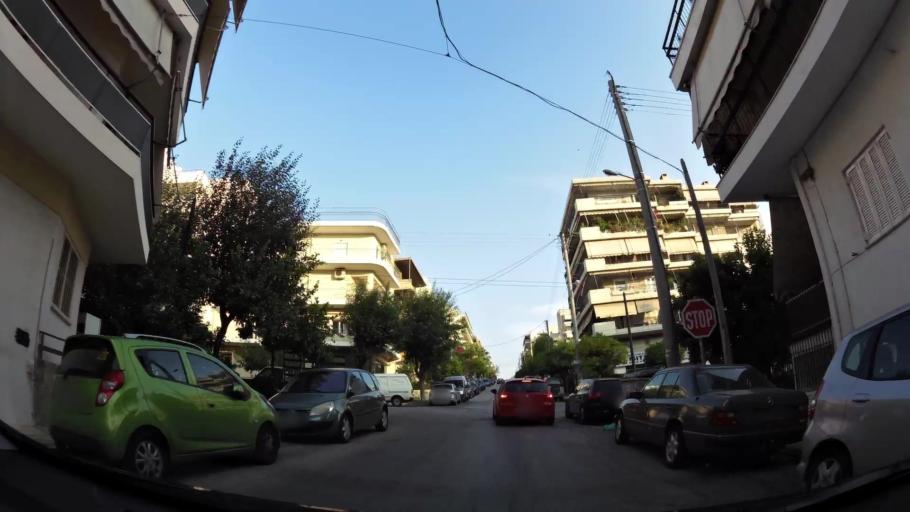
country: GR
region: Attica
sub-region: Nomarchia Athinas
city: Galatsi
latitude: 38.0237
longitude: 23.7543
